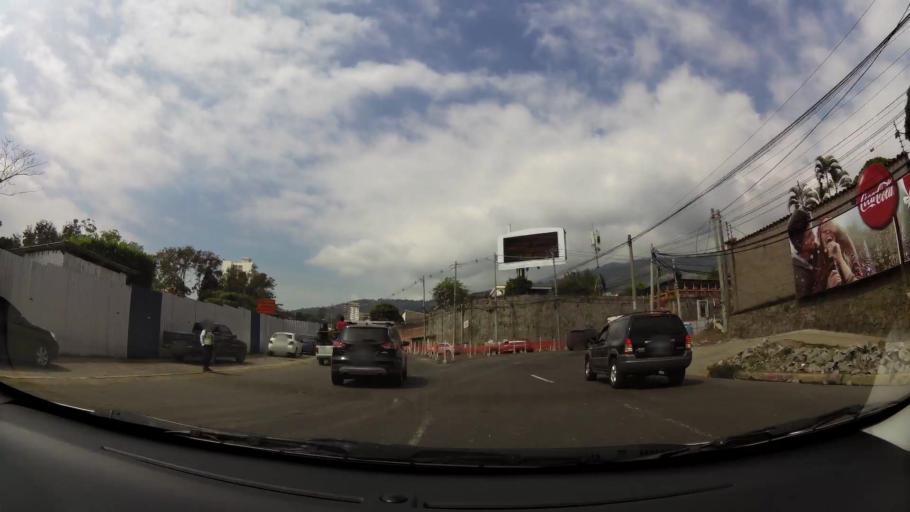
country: SV
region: La Libertad
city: Antiguo Cuscatlan
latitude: 13.7041
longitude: -89.2490
